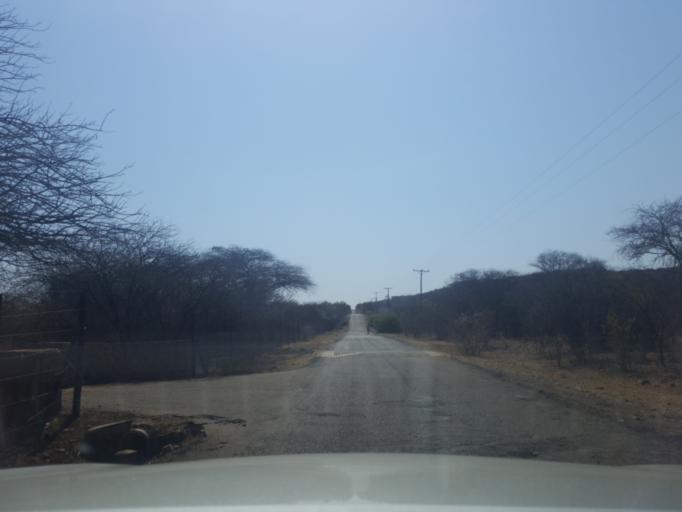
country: BW
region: Kweneng
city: Gabane
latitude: -24.7437
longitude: 25.8268
